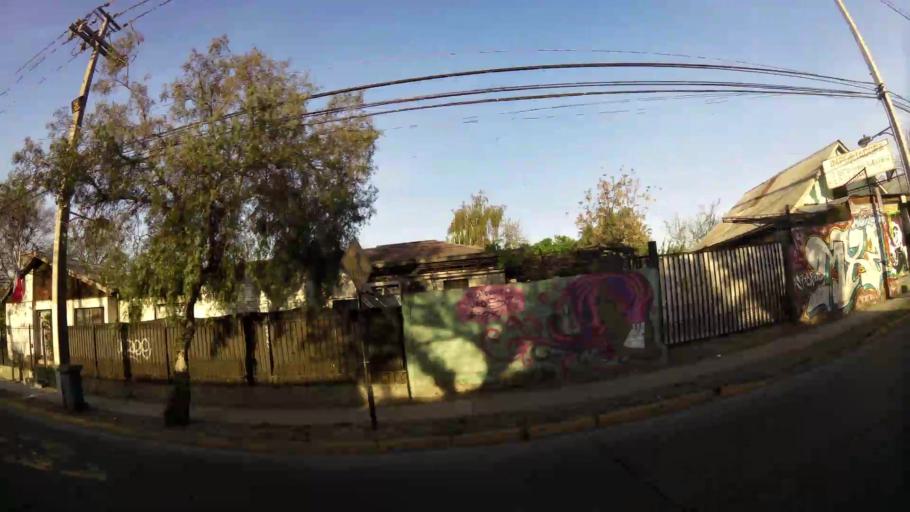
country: CL
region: Santiago Metropolitan
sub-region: Provincia de Santiago
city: La Pintana
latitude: -33.5495
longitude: -70.5829
